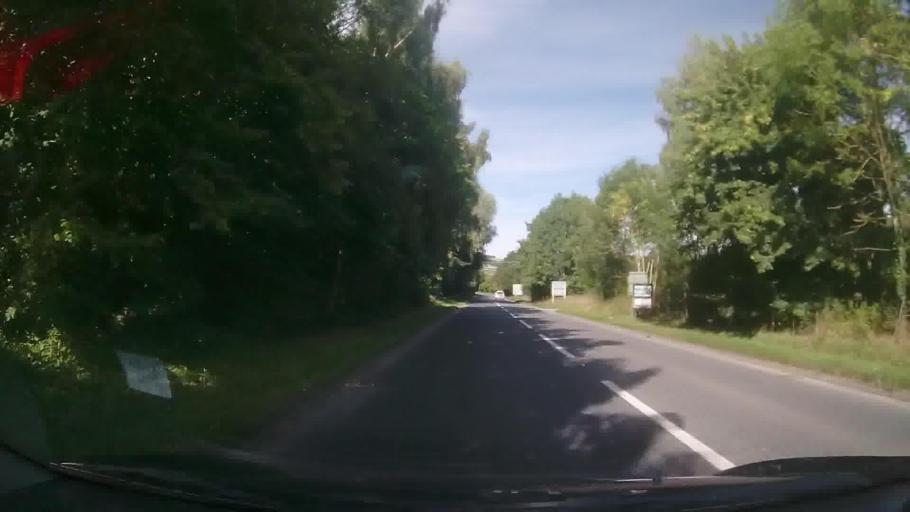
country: GB
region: England
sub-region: Herefordshire
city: Kington
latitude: 52.2020
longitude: -3.0203
